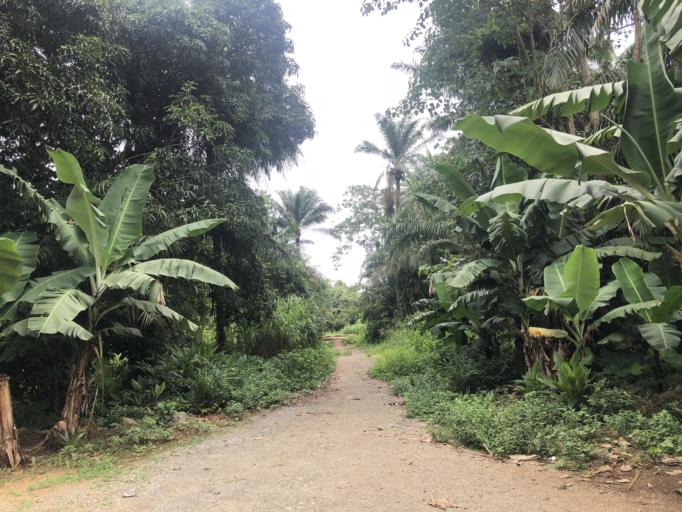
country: SL
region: Northern Province
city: Bumbuna
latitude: 8.9910
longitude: -11.7531
